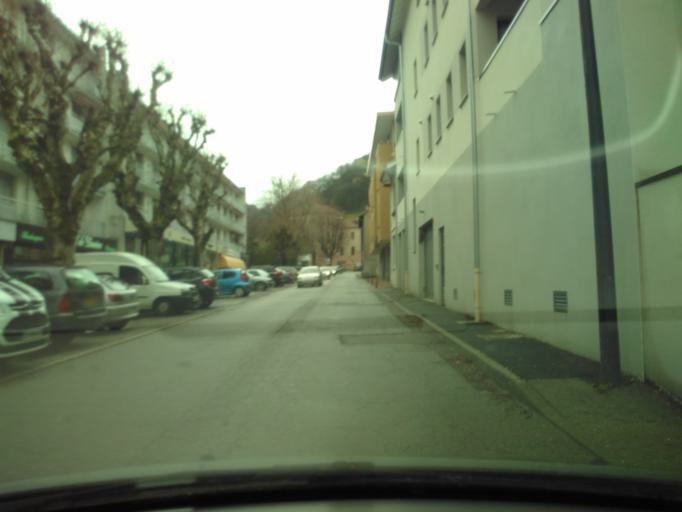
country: FR
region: Rhone-Alpes
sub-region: Departement de l'Isere
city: Domene
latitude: 45.2034
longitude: 5.8372
